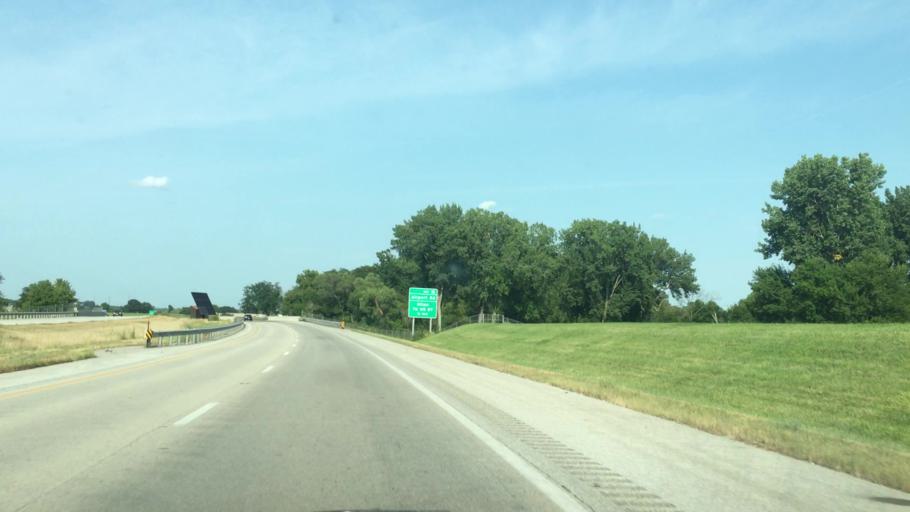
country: US
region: Illinois
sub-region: Rock Island County
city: Milan
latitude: 41.4468
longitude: -90.5582
